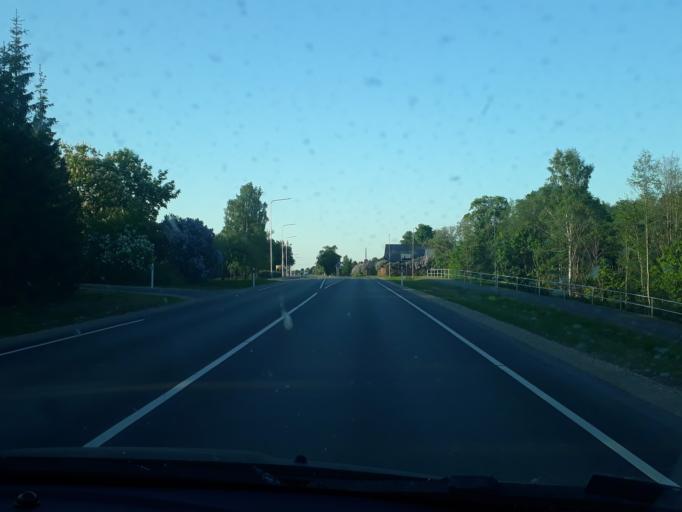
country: EE
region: Paernumaa
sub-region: Tootsi vald
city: Tootsi
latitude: 58.5148
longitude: 24.8160
